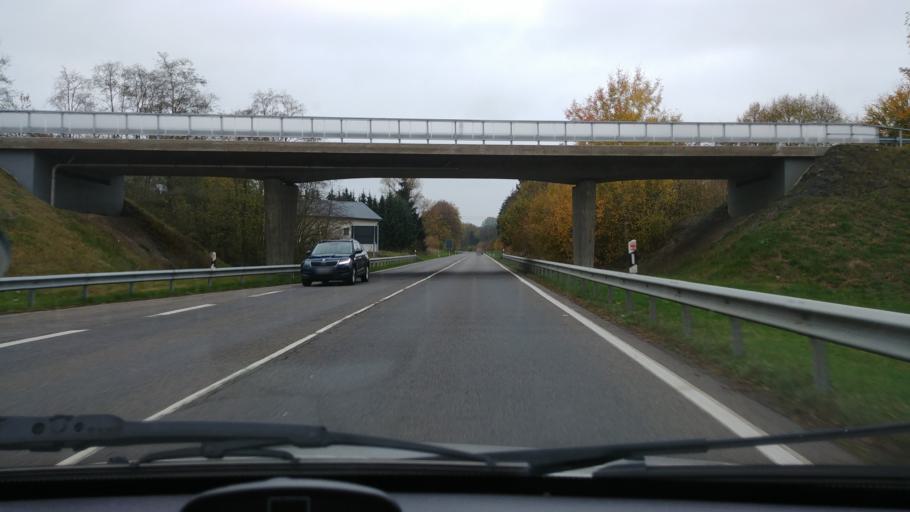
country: DE
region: Rheinland-Pfalz
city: Enspel
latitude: 50.6275
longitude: 7.8876
